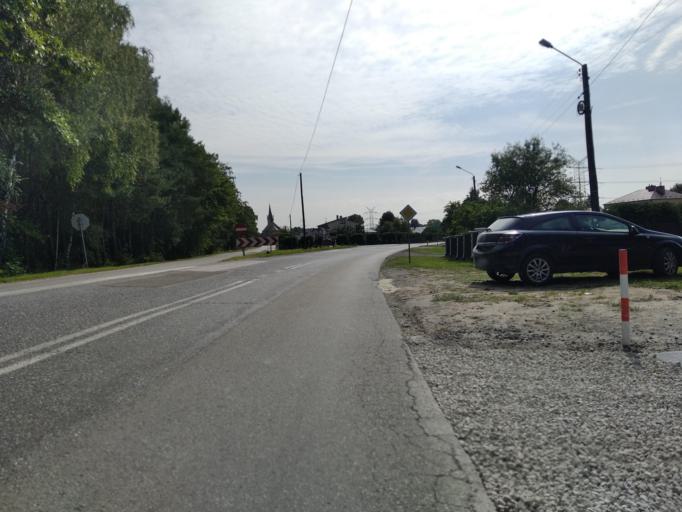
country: PL
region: Subcarpathian Voivodeship
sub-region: Powiat ropczycko-sedziszowski
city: Ostrow
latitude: 50.1430
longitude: 21.5827
